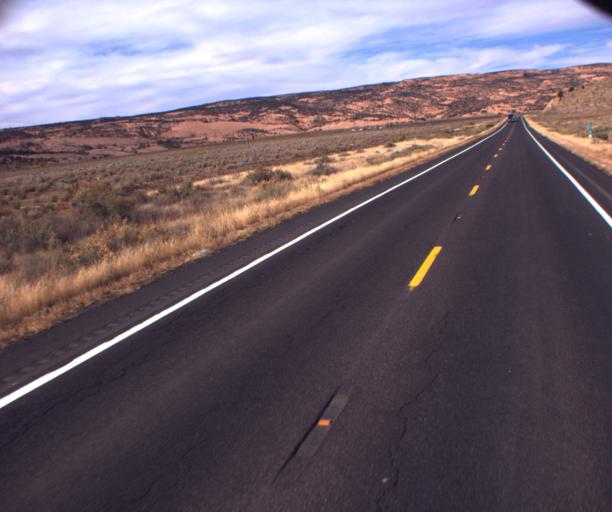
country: US
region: Arizona
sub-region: Navajo County
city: Kayenta
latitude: 36.6022
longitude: -110.4727
